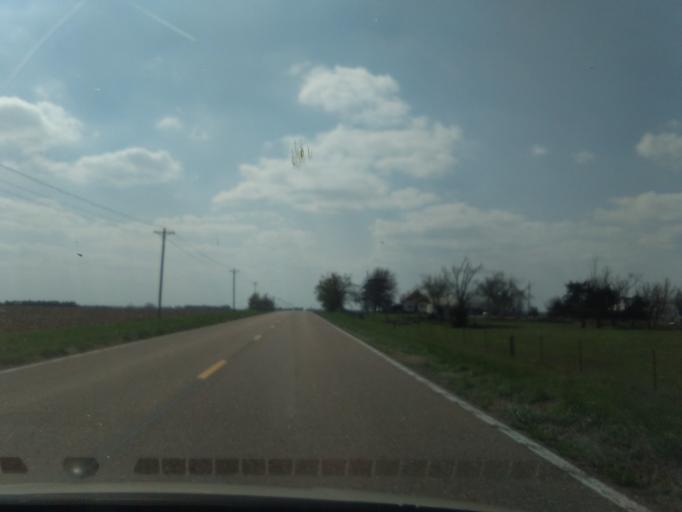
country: US
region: Nebraska
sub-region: Nuckolls County
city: Nelson
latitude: 40.1471
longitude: -97.9060
